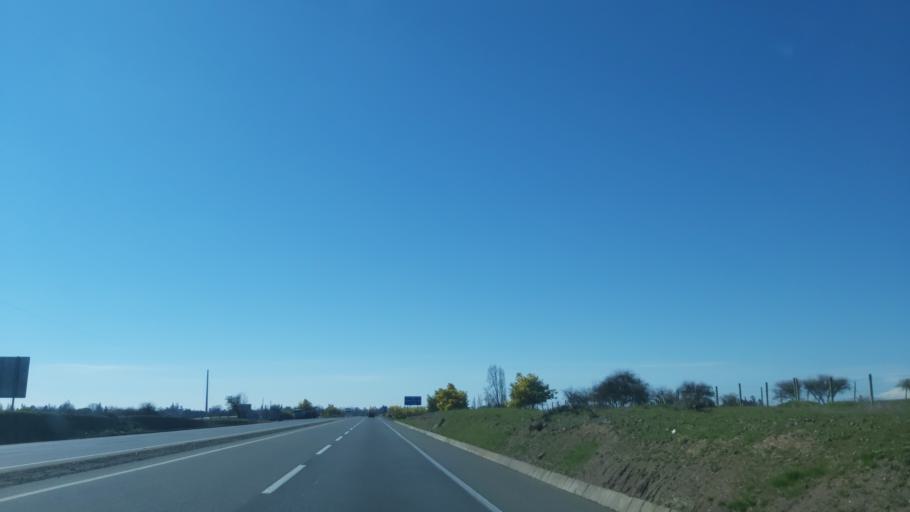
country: CL
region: Biobio
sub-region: Provincia de Nuble
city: Bulnes
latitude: -36.6562
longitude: -72.2449
